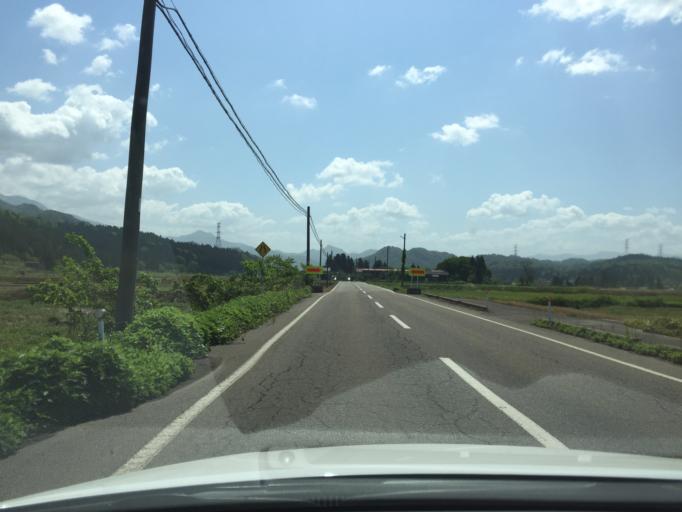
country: JP
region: Niigata
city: Tochio-honcho
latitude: 37.5518
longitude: 139.0818
